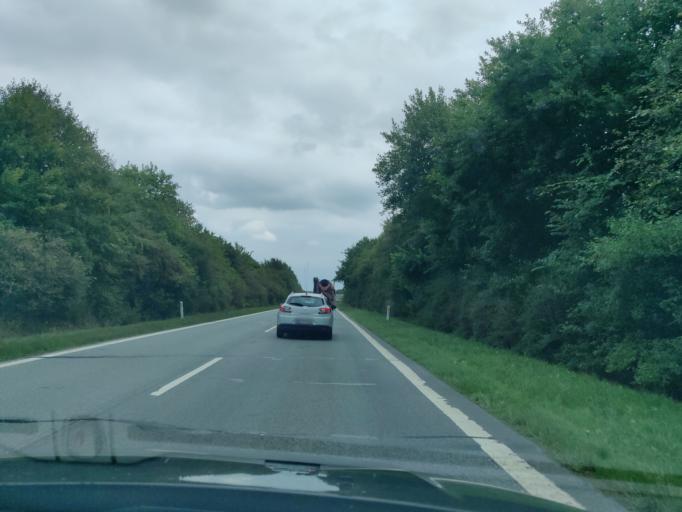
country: DK
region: North Denmark
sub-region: Alborg Kommune
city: Frejlev
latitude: 57.0122
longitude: 9.7649
